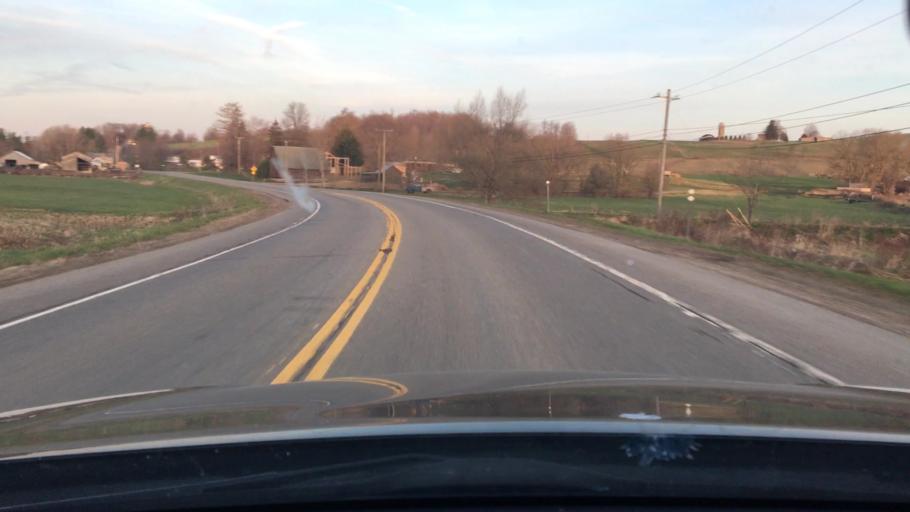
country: US
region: New York
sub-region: Cattaraugus County
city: Randolph
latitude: 42.1947
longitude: -78.9094
